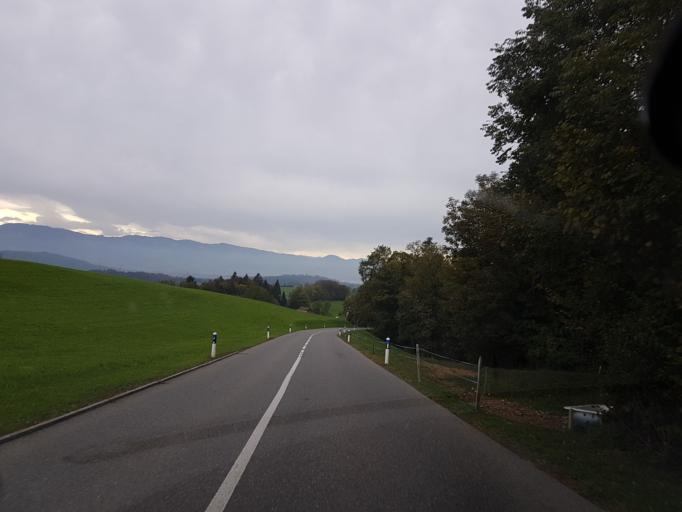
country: CH
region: Saint Gallen
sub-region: Wahlkreis See-Gaster
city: Goldingen
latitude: 47.2519
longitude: 8.9555
